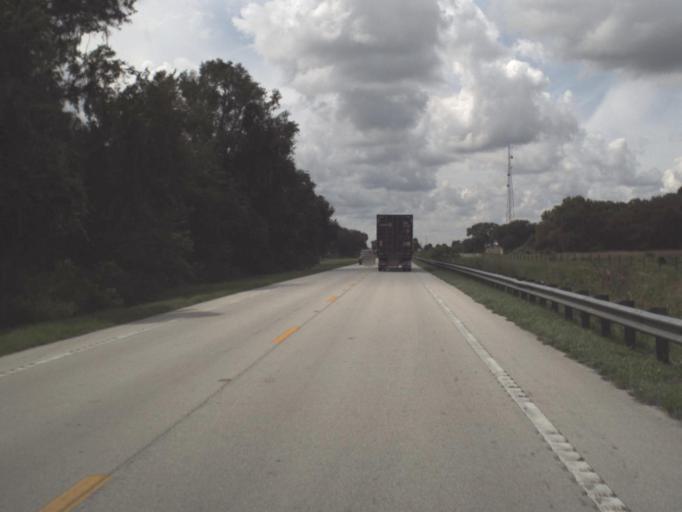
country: US
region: Florida
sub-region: Glades County
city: Buckhead Ridge
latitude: 27.2290
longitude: -81.0895
